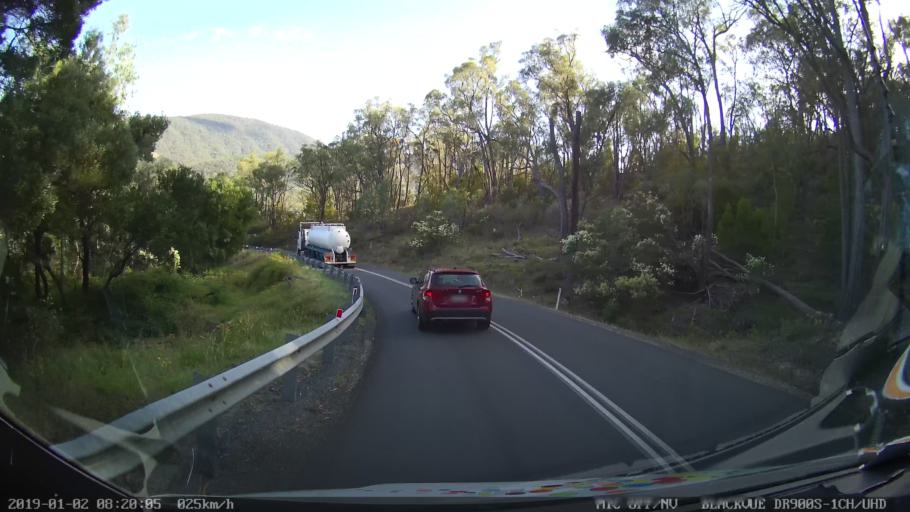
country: AU
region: New South Wales
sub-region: Tumut Shire
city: Tumut
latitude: -35.5737
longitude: 148.3240
